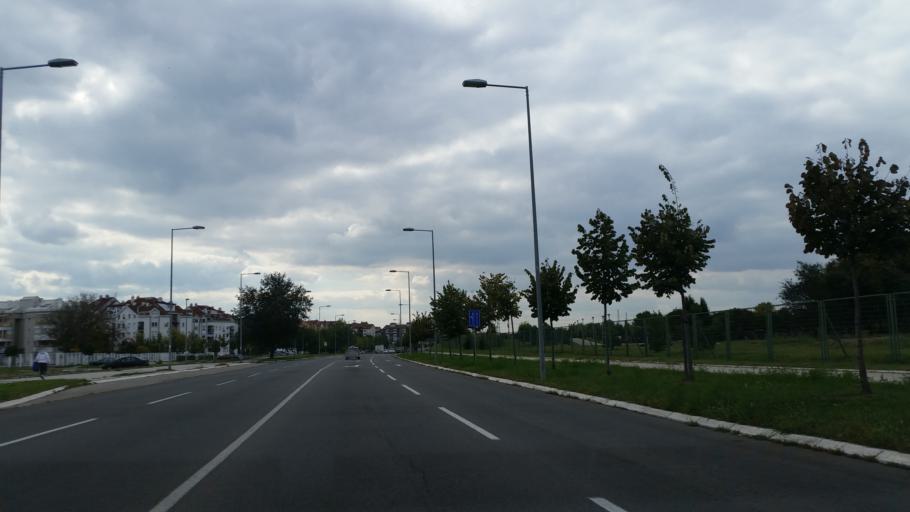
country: RS
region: Central Serbia
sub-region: Belgrade
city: Zemun
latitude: 44.8149
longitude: 20.3691
